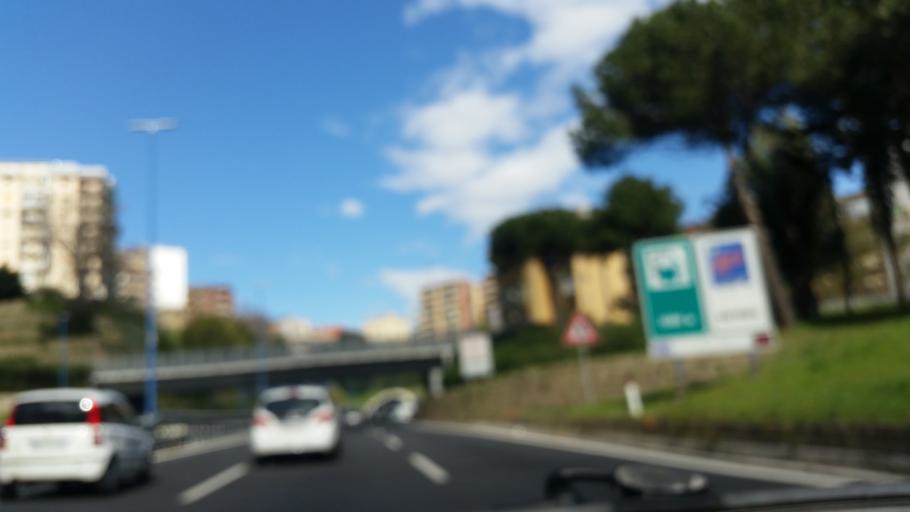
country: IT
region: Campania
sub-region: Provincia di Napoli
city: Napoli
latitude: 40.8553
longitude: 14.2199
